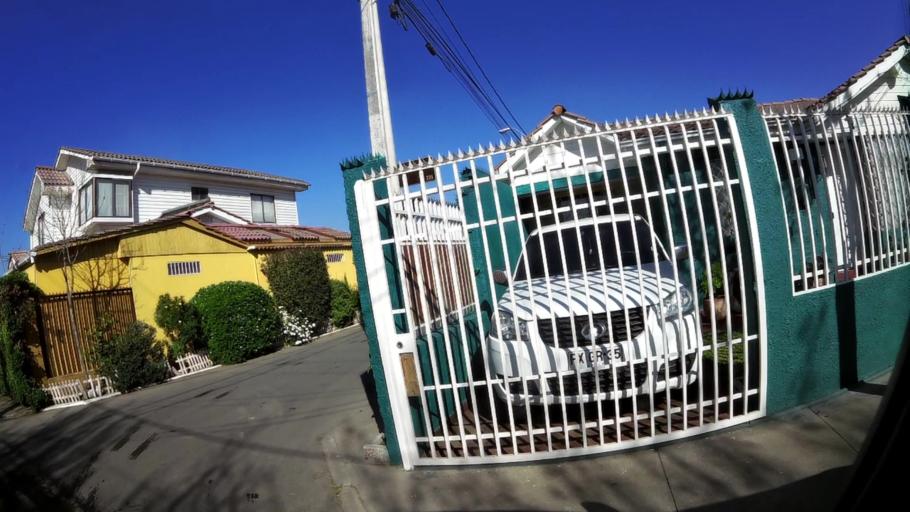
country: CL
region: Santiago Metropolitan
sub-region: Provincia de Santiago
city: Lo Prado
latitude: -33.4890
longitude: -70.7800
